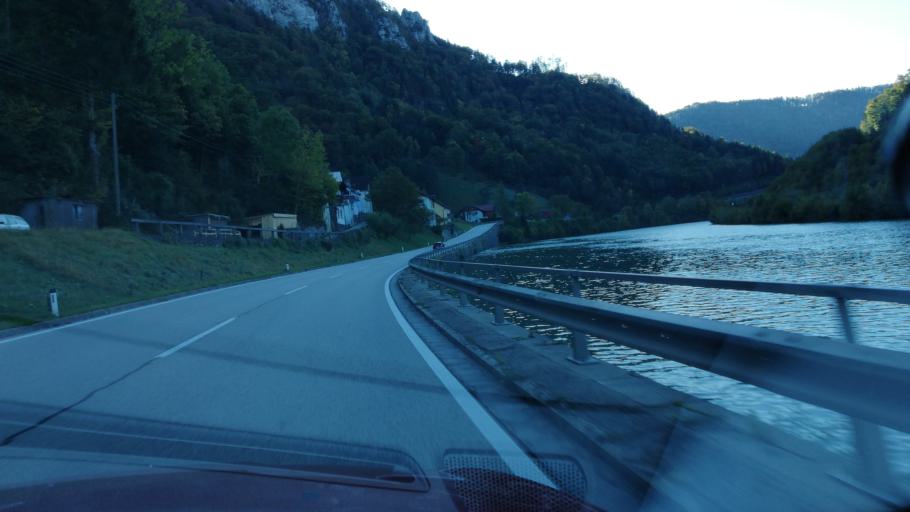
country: AT
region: Upper Austria
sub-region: Politischer Bezirk Steyr-Land
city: Losenstein
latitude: 47.9131
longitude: 14.4487
